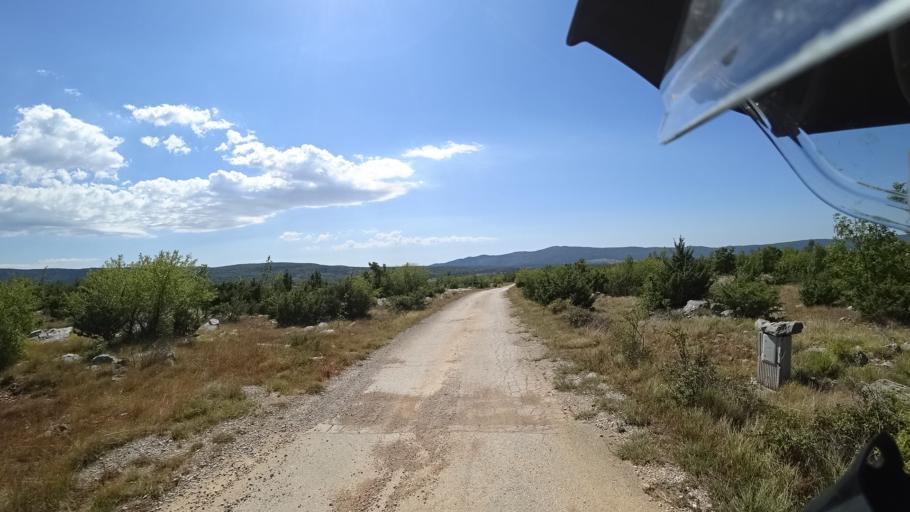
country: HR
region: Splitsko-Dalmatinska
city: Hrvace
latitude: 43.7518
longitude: 16.4421
